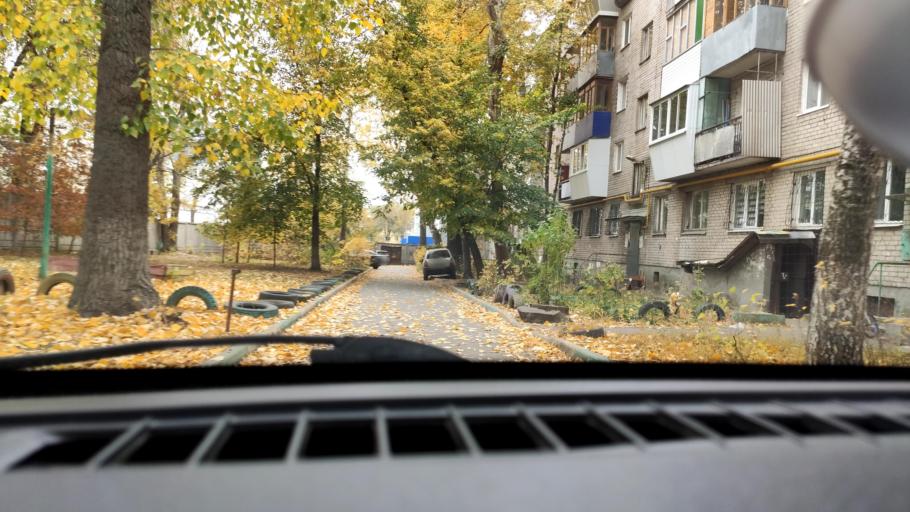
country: RU
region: Samara
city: Samara
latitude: 53.1931
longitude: 50.1882
